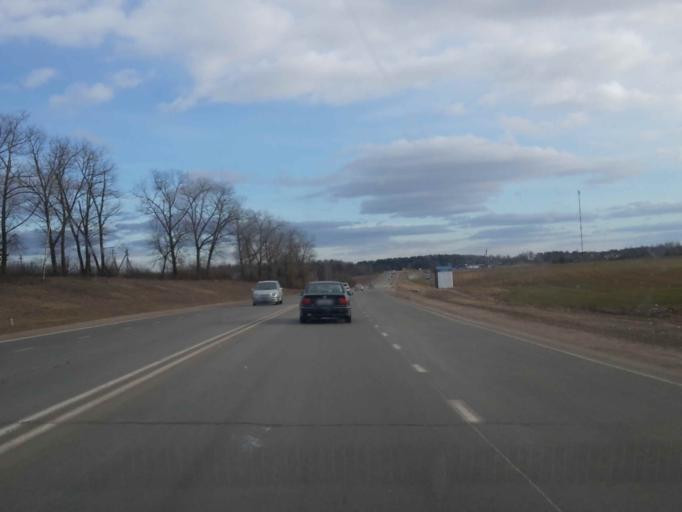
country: BY
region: Minsk
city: Bal'shavik
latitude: 54.0778
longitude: 27.5636
